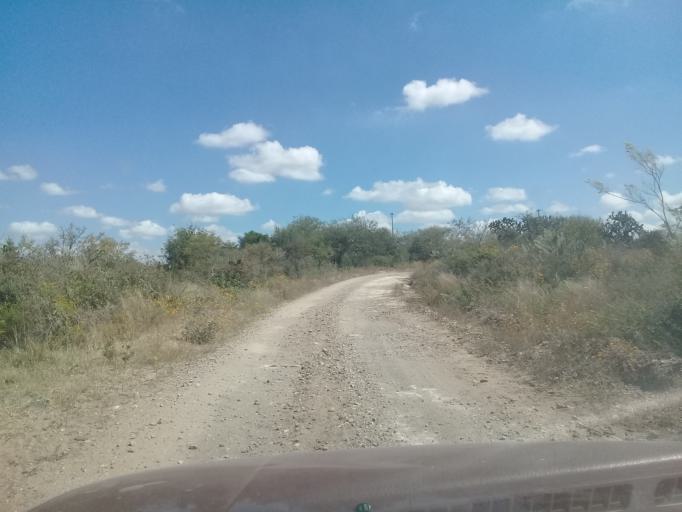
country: MX
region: Aguascalientes
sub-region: Aguascalientes
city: San Sebastian [Fraccionamiento]
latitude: 21.7795
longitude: -102.2518
